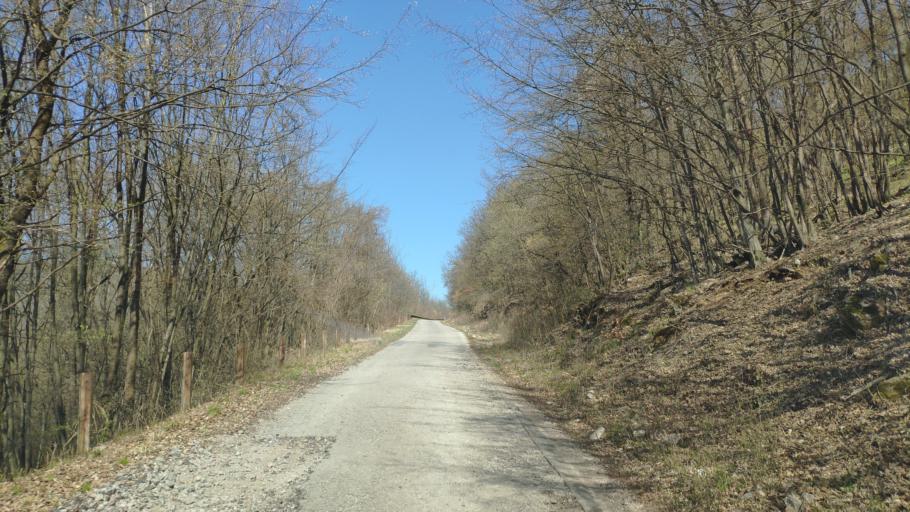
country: SK
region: Kosicky
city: Roznava
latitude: 48.5613
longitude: 20.4042
